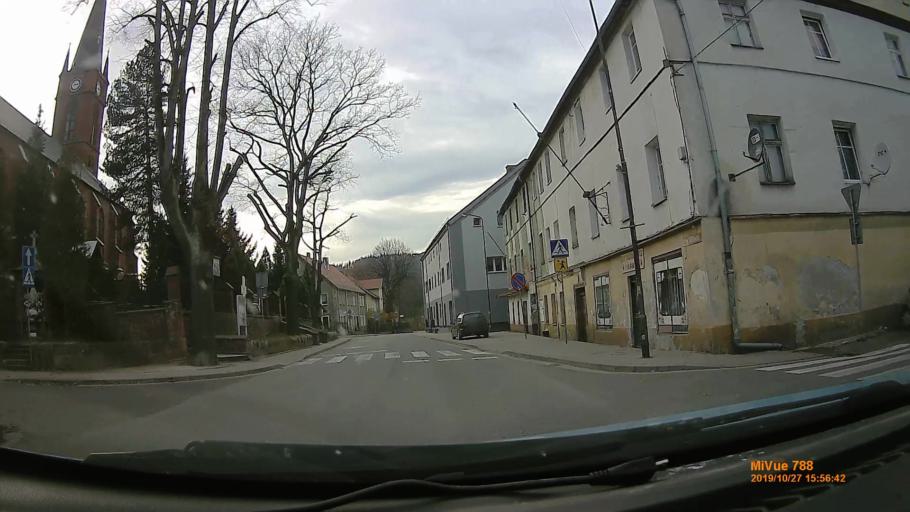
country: PL
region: Lower Silesian Voivodeship
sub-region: Powiat klodzki
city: Bozkow
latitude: 50.5448
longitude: 16.5468
